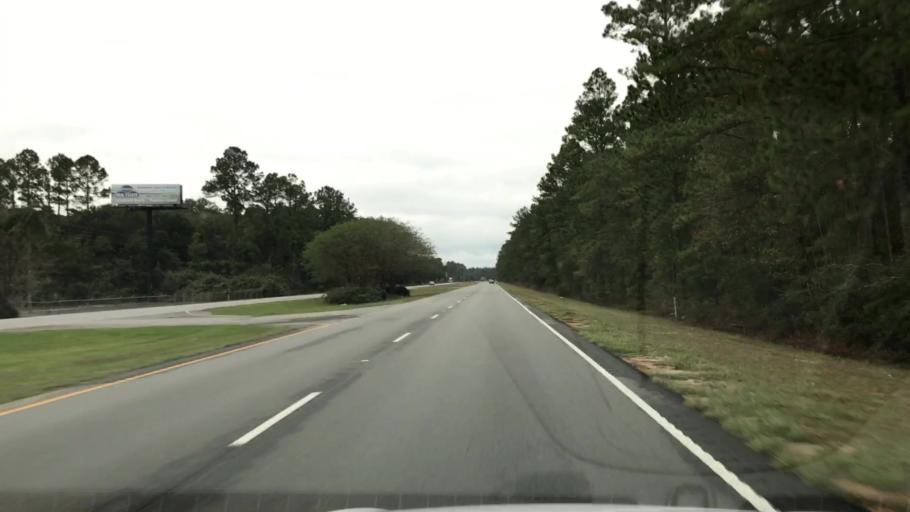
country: US
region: South Carolina
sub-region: Georgetown County
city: Georgetown
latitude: 33.2362
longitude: -79.3758
